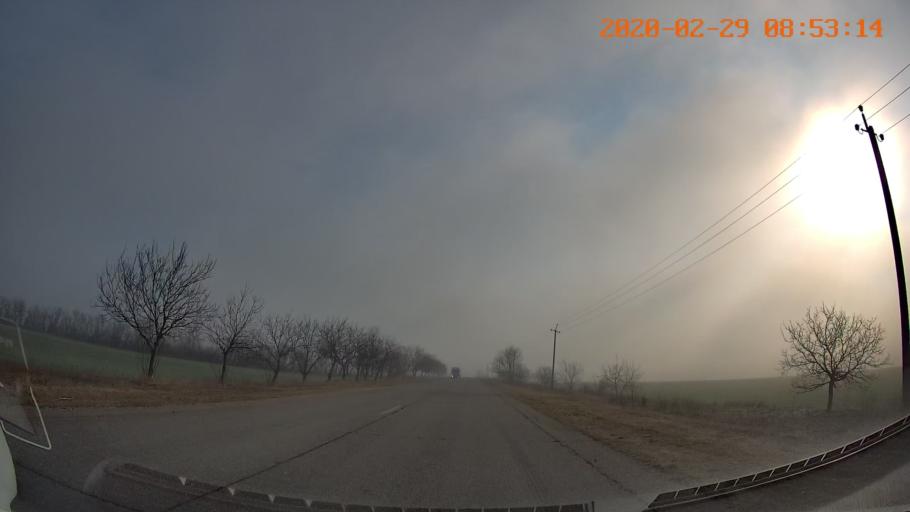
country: MD
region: Telenesti
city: Tiraspolul Nou
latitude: 46.9253
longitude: 29.5528
